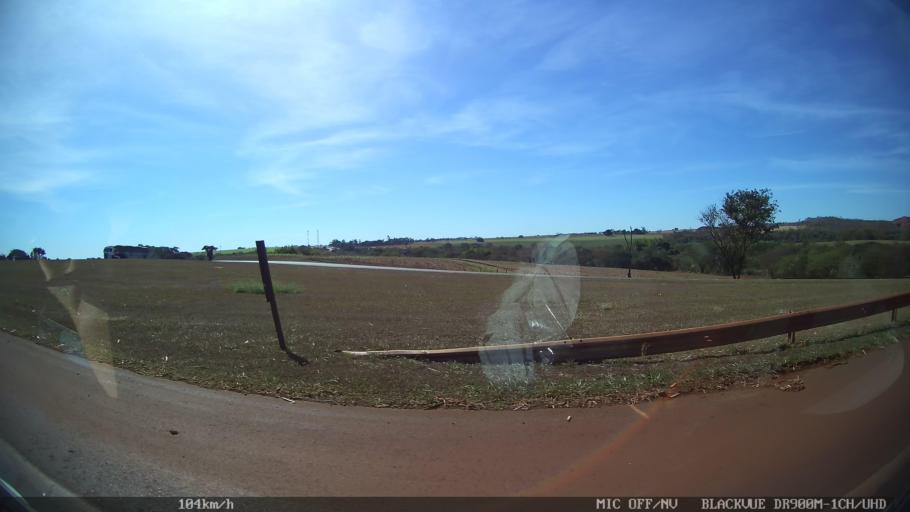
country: BR
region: Sao Paulo
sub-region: Sao Joaquim Da Barra
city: Sao Joaquim da Barra
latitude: -20.5253
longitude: -47.8383
